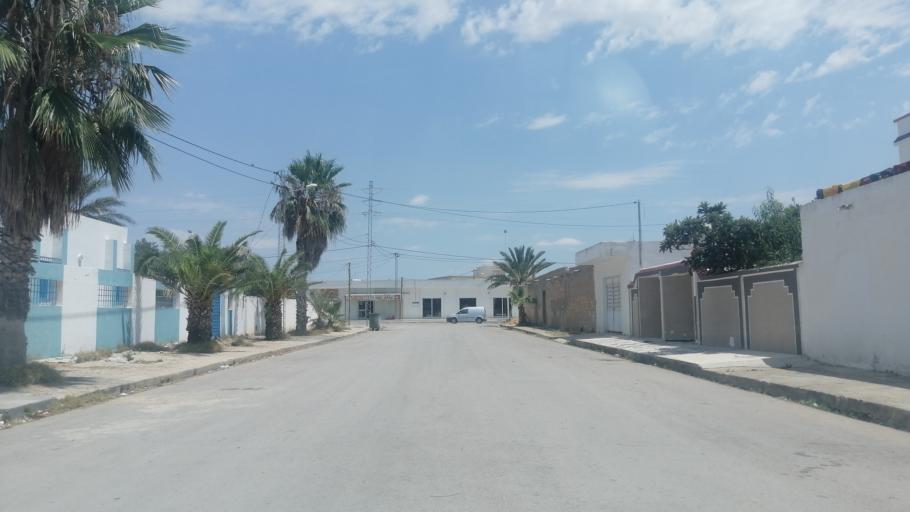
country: TN
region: Al Qayrawan
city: Sbikha
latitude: 36.1222
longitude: 10.0935
